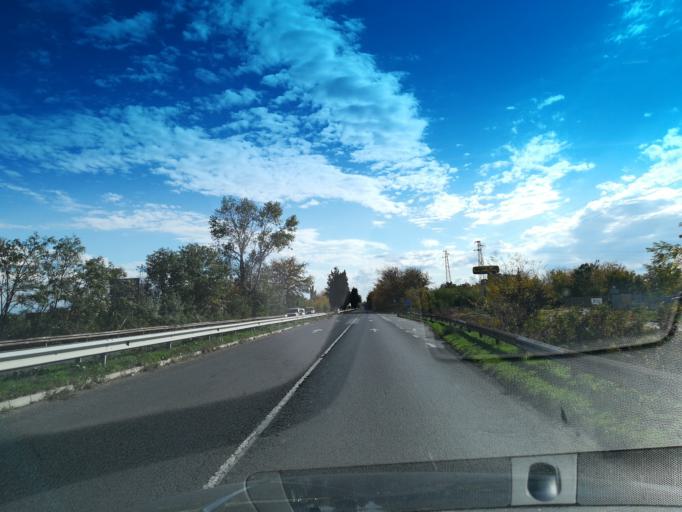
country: BG
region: Stara Zagora
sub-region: Obshtina Stara Zagora
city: Stara Zagora
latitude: 42.3893
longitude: 25.6474
